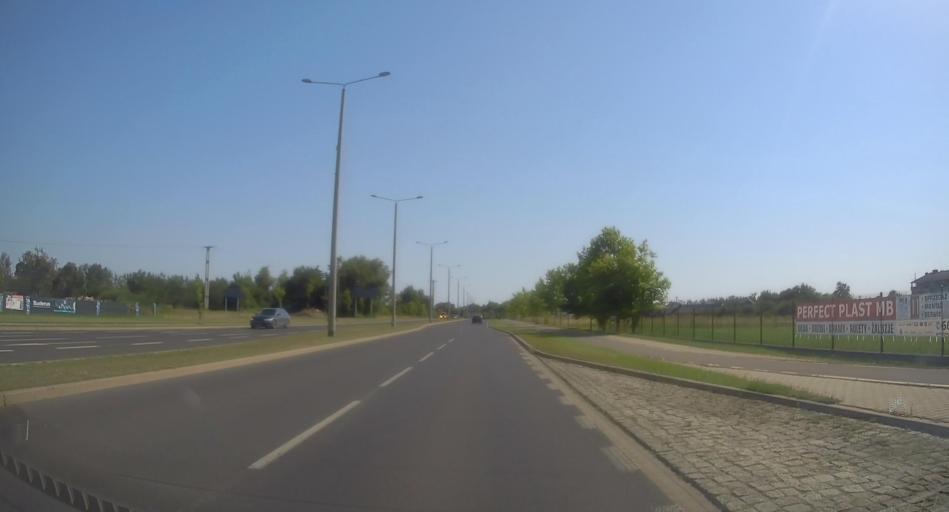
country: PL
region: Lodz Voivodeship
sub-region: Skierniewice
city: Skierniewice
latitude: 51.9474
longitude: 20.1588
